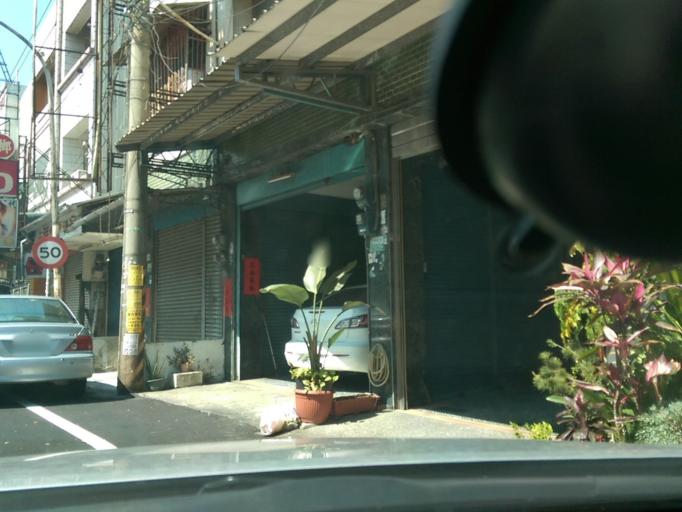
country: TW
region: Taiwan
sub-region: Chiayi
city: Jiayi Shi
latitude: 23.4513
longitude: 120.4602
